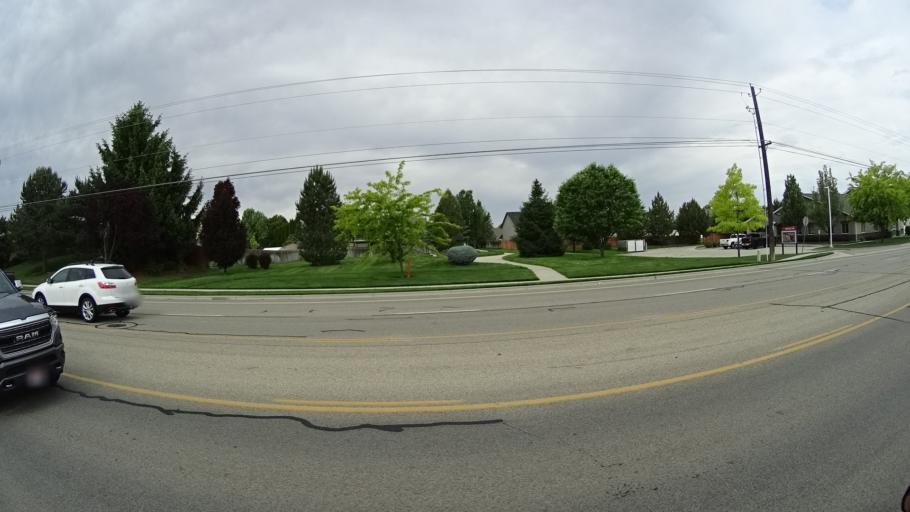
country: US
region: Idaho
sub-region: Ada County
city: Meridian
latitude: 43.5816
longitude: -116.3544
